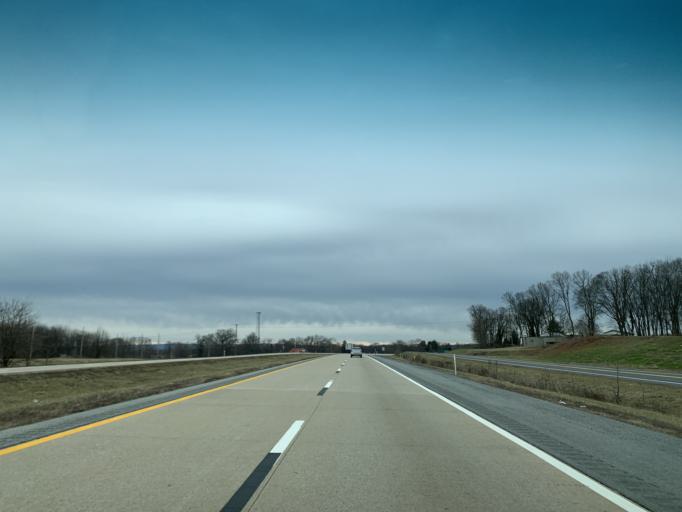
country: US
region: West Virginia
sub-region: Jefferson County
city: Ranson
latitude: 39.3561
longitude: -77.8589
